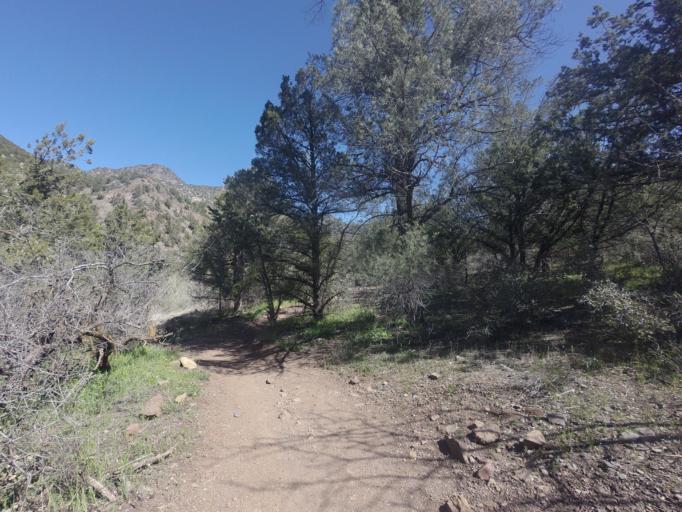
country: US
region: Arizona
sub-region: Gila County
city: Pine
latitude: 34.4070
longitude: -111.6097
